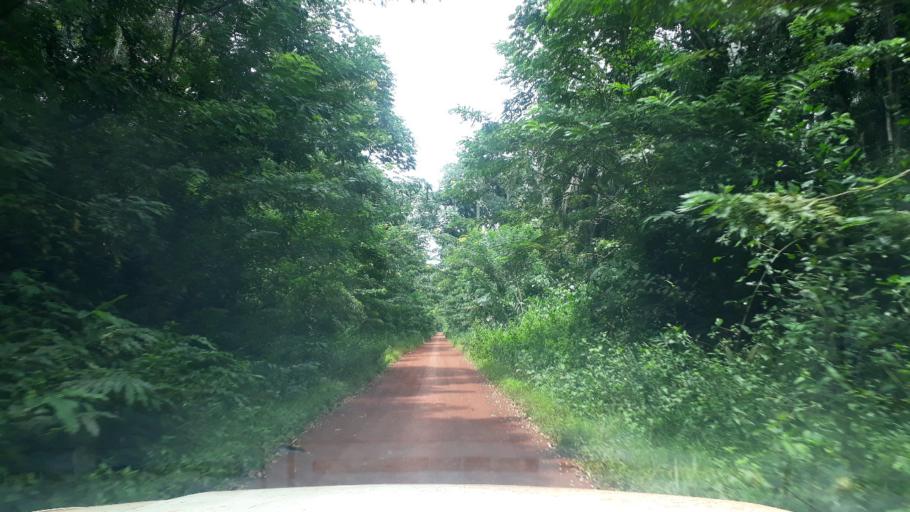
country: CD
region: Eastern Province
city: Aketi
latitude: 2.9270
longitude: 24.0853
